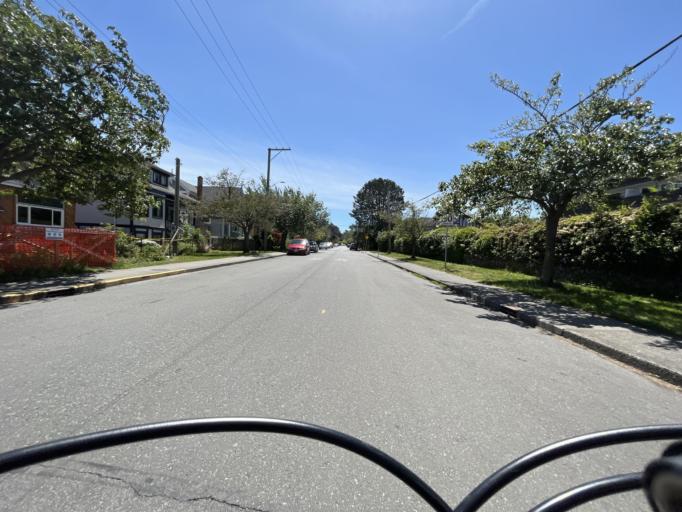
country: CA
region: British Columbia
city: Victoria
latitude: 48.4148
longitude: -123.3594
